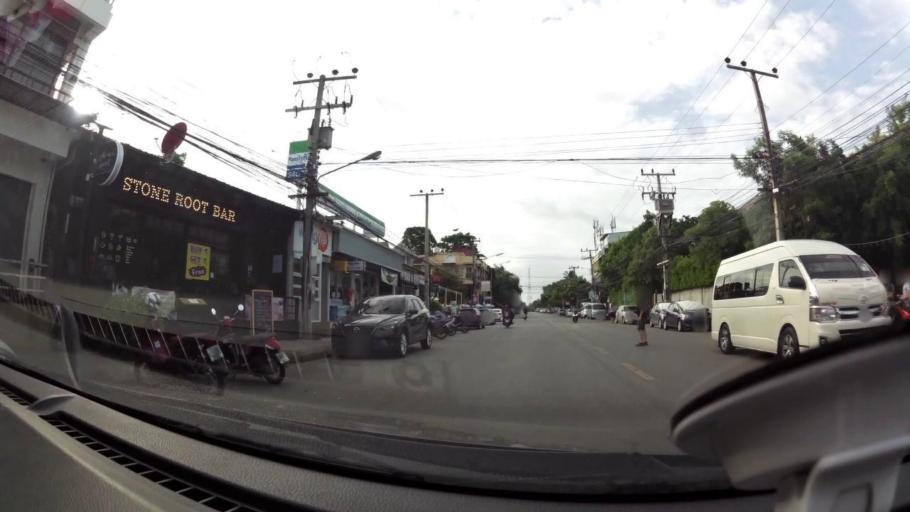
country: TH
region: Prachuap Khiri Khan
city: Hua Hin
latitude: 12.5788
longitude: 99.9561
